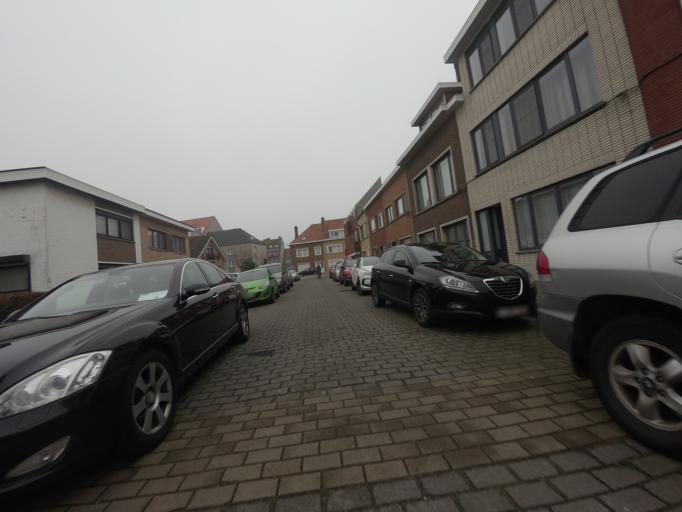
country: BE
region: Flanders
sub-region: Provincie West-Vlaanderen
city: Ostend
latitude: 51.2126
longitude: 2.8803
